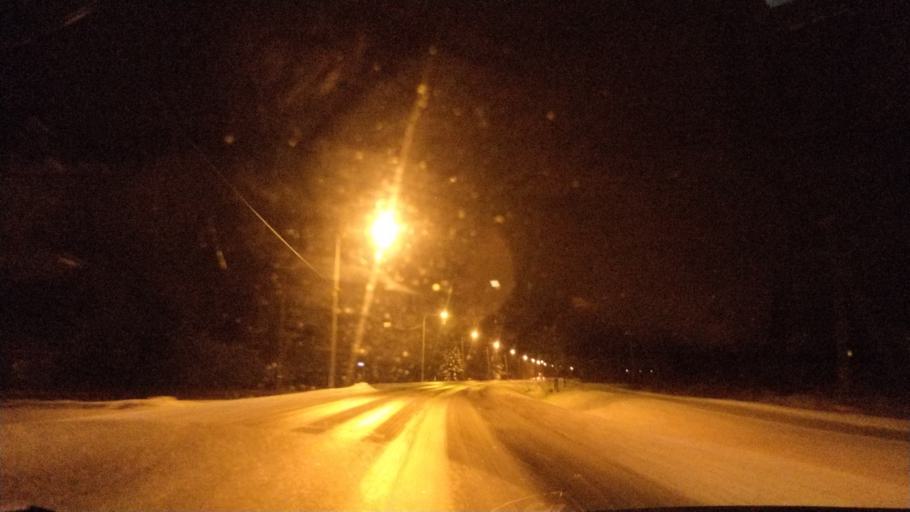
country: FI
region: Lapland
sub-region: Rovaniemi
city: Rovaniemi
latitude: 66.3166
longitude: 25.3616
